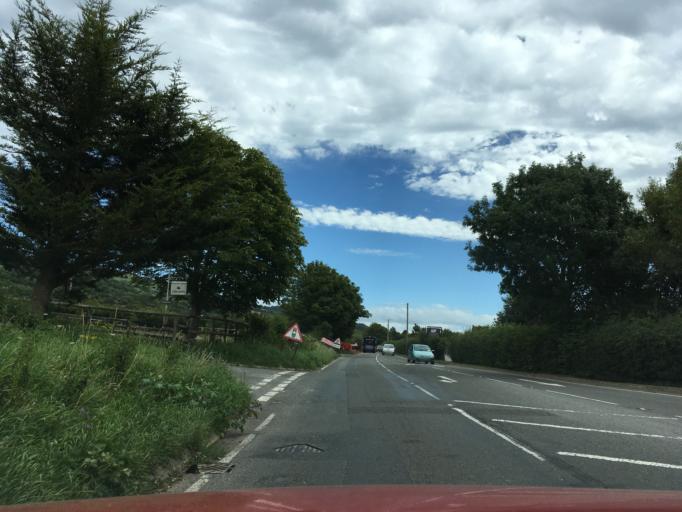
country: GB
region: England
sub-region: Somerset
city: Bradley Cross
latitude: 51.2666
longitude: -2.7674
